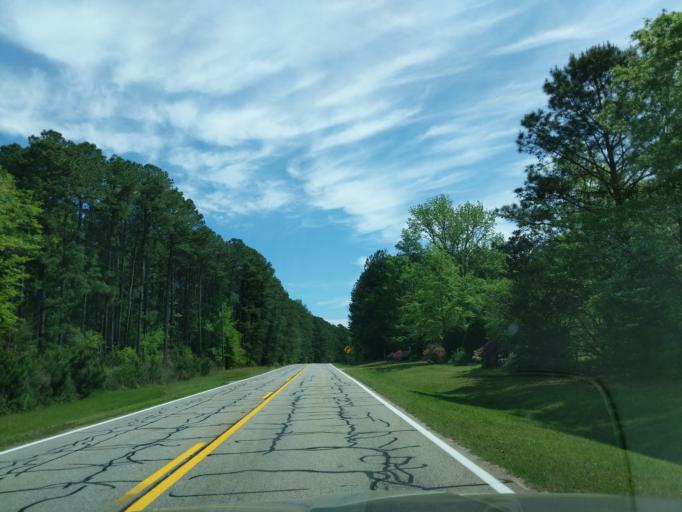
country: US
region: Georgia
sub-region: Columbia County
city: Appling
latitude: 33.6105
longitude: -82.3408
